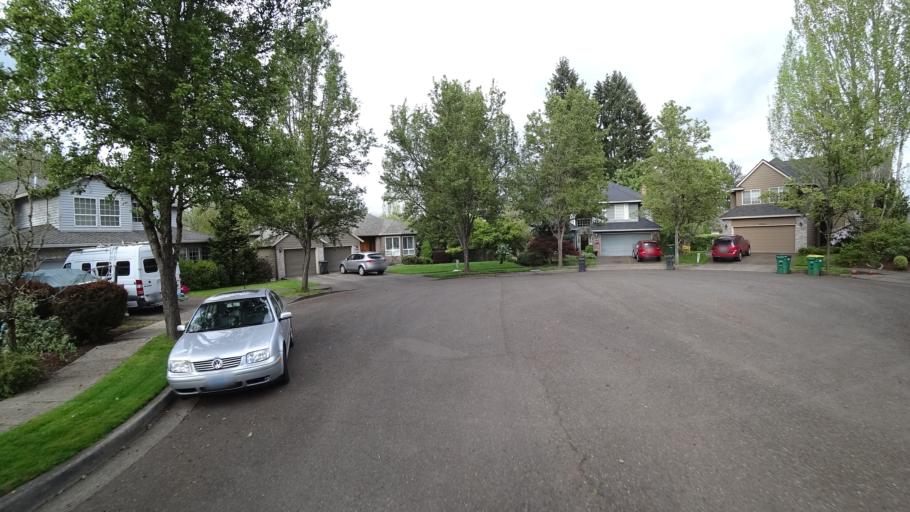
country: US
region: Oregon
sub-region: Washington County
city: Aloha
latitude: 45.4567
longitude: -122.8397
